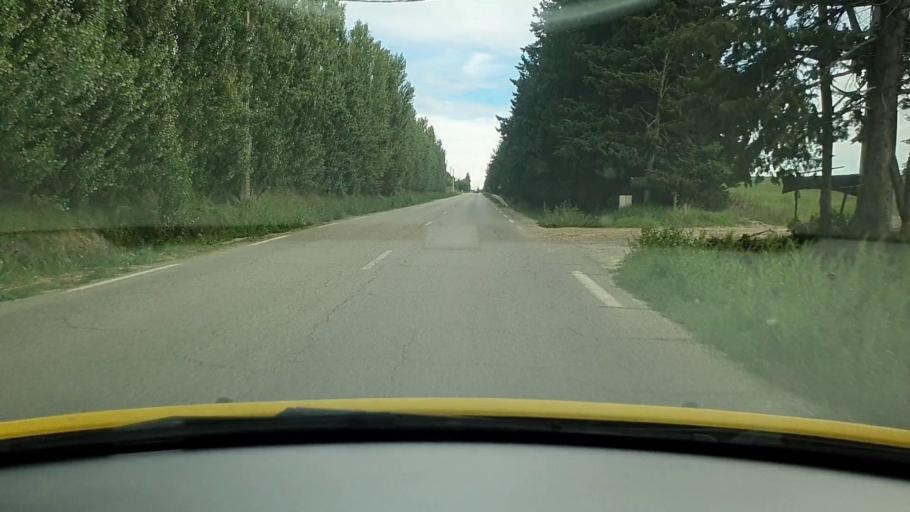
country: FR
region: Languedoc-Roussillon
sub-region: Departement du Gard
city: Saint-Gilles
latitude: 43.7005
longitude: 4.4503
